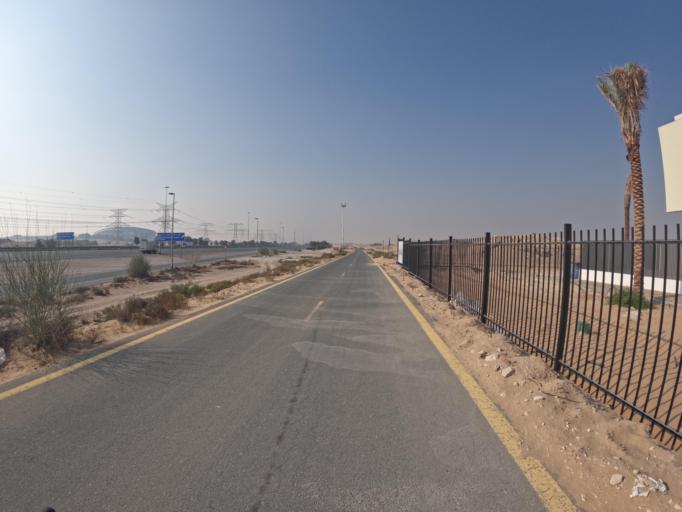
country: AE
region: Dubai
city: Dubai
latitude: 25.0594
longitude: 55.3202
